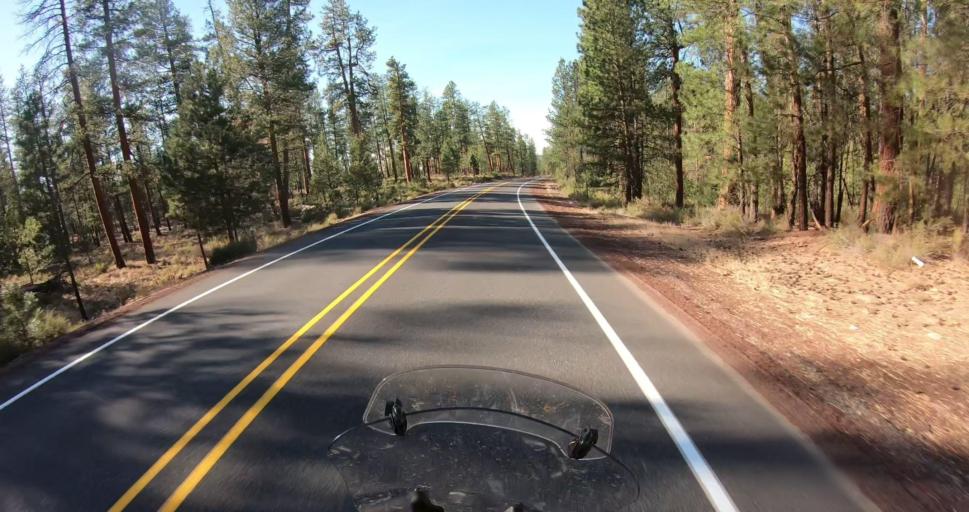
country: US
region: Oregon
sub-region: Deschutes County
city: La Pine
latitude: 43.4692
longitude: -121.3980
